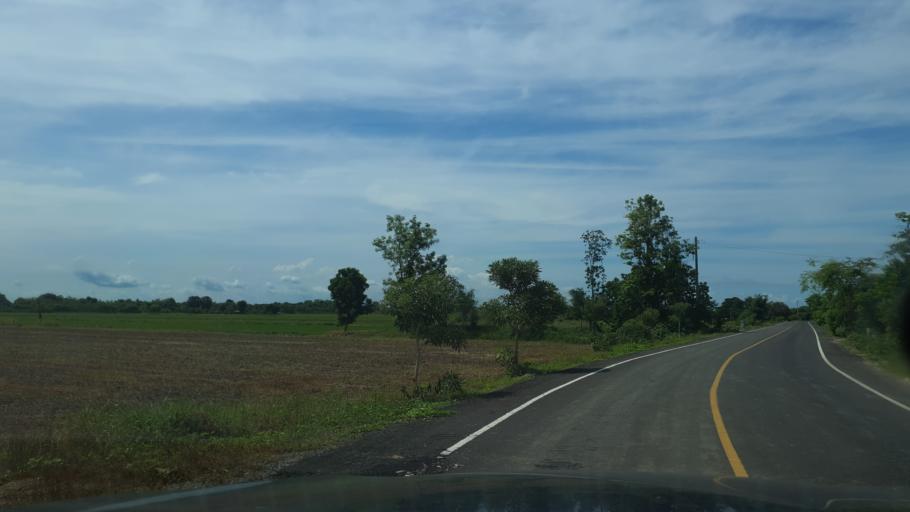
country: TH
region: Sukhothai
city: Si Samrong
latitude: 17.1945
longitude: 99.7379
